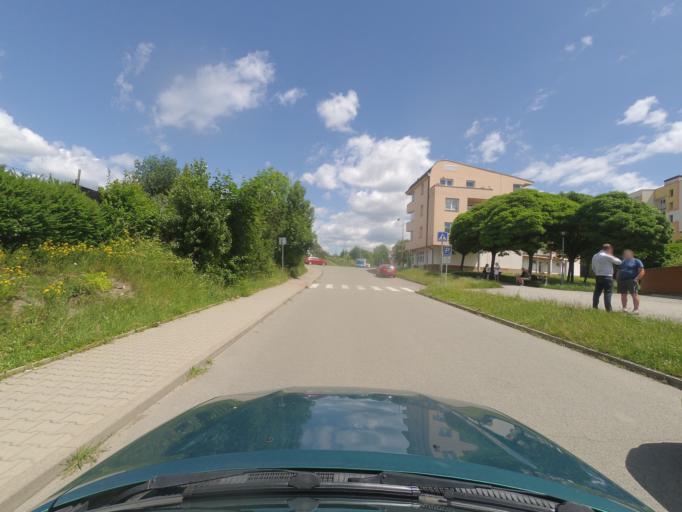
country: CZ
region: Kralovehradecky
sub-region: Okres Rychnov nad Kneznou
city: Rychnov nad Kneznou
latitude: 50.1638
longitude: 16.2827
